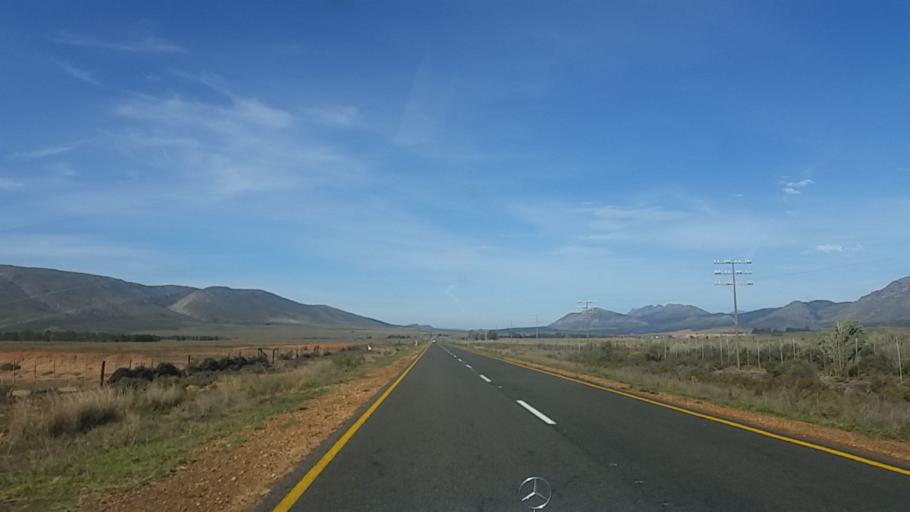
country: ZA
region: Western Cape
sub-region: Eden District Municipality
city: George
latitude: -33.8109
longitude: 22.5395
